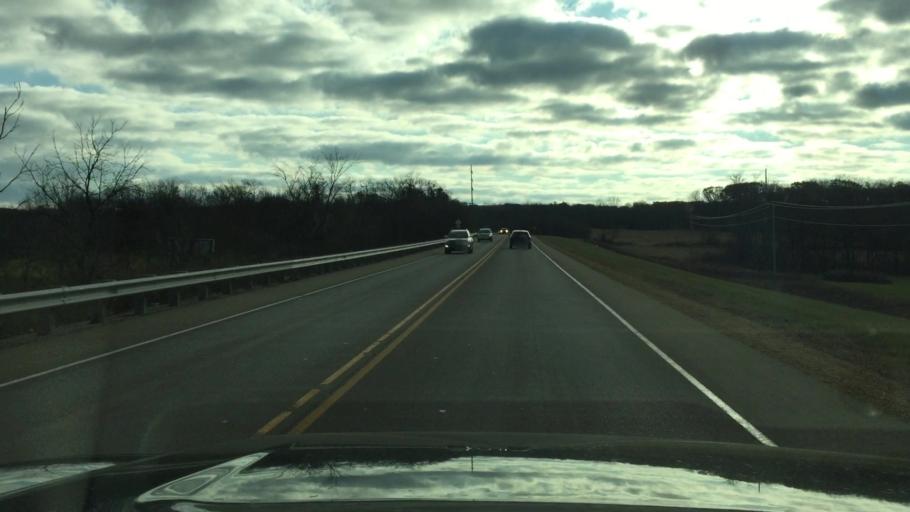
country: US
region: Wisconsin
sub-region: Walworth County
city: Williams Bay
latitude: 42.5859
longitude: -88.5281
